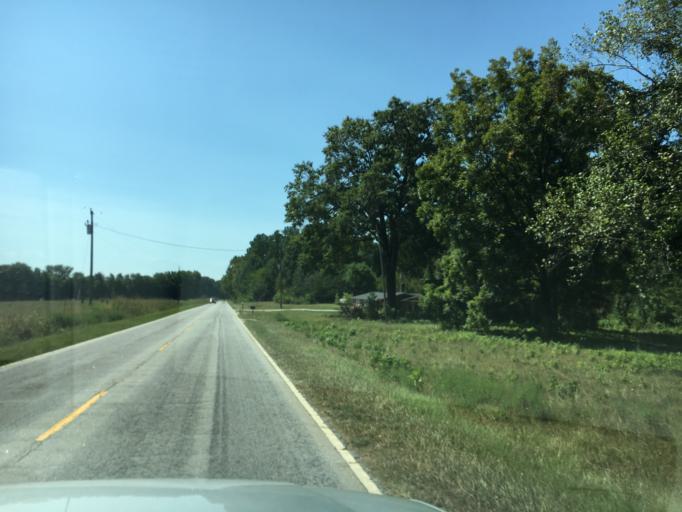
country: US
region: South Carolina
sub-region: Laurens County
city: Joanna
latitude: 34.2969
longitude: -81.8443
